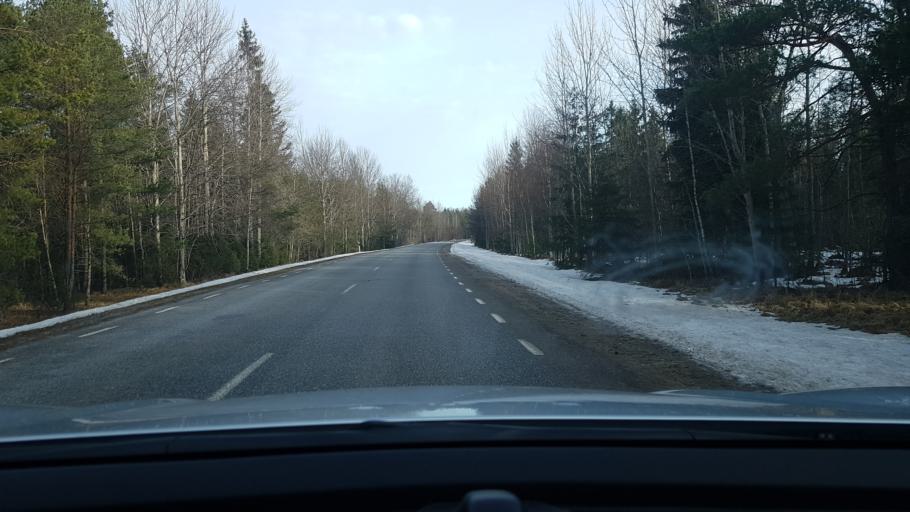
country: EE
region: Saare
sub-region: Kuressaare linn
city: Kuressaare
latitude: 58.4212
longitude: 22.6662
